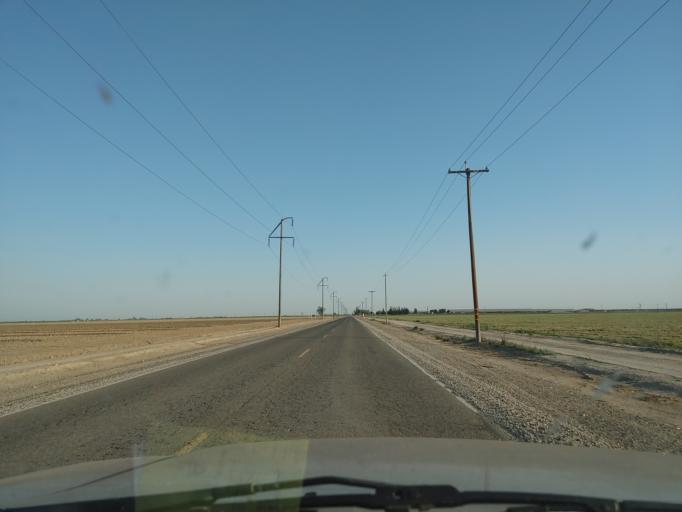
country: US
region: California
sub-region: Madera County
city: Chowchilla
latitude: 37.1697
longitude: -120.3831
